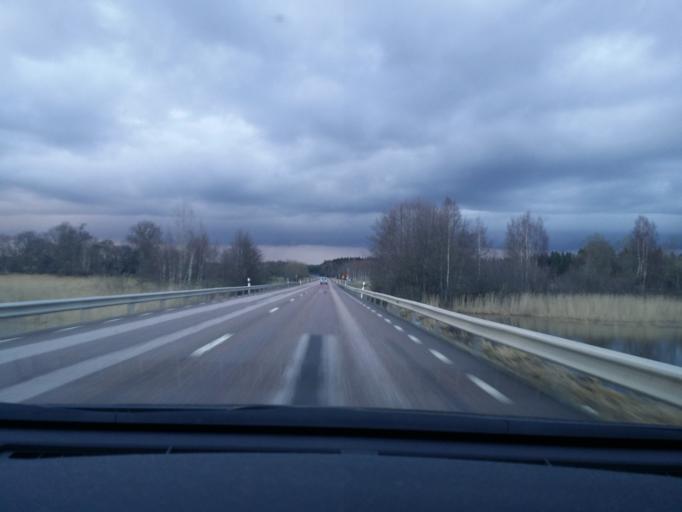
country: SE
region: Soedermanland
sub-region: Eskilstuna Kommun
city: Kvicksund
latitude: 59.4810
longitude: 16.3051
